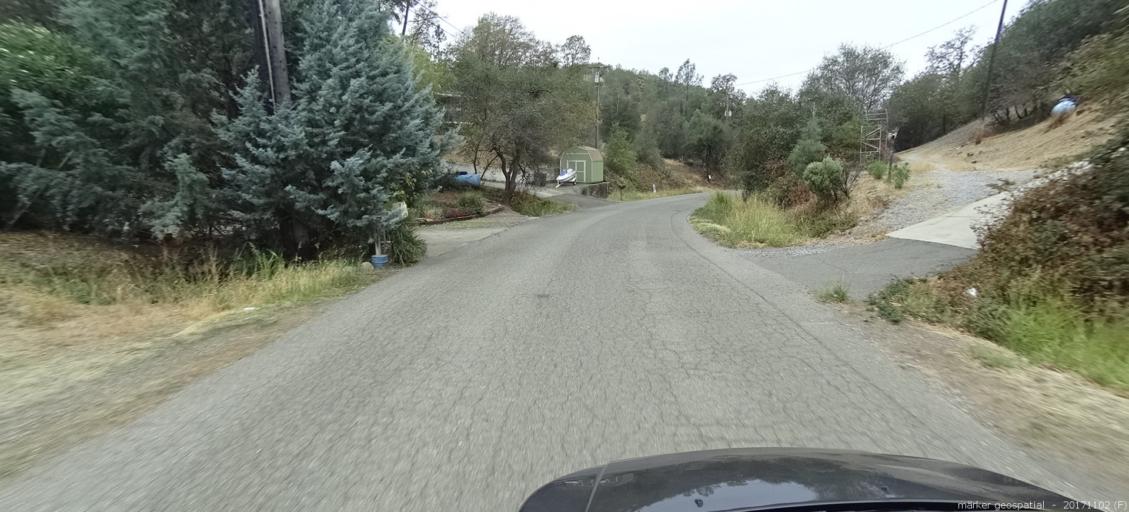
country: US
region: California
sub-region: Shasta County
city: Bella Vista
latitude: 40.7144
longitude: -122.2363
